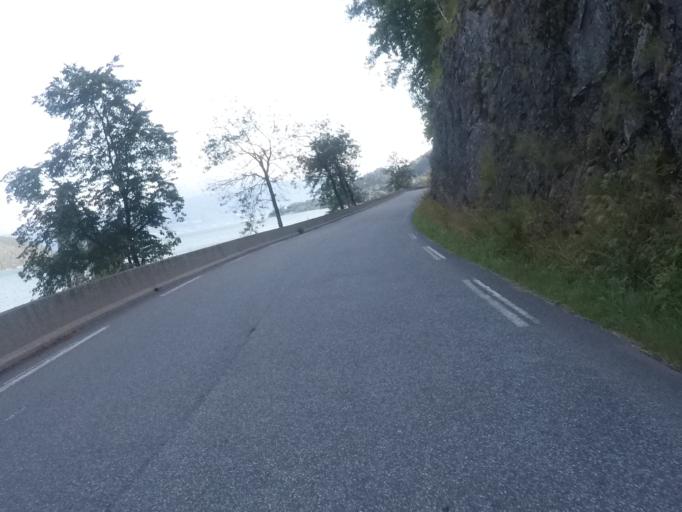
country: NO
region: Sogn og Fjordane
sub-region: Balestrand
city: Balestrand
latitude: 61.2375
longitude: 6.5516
